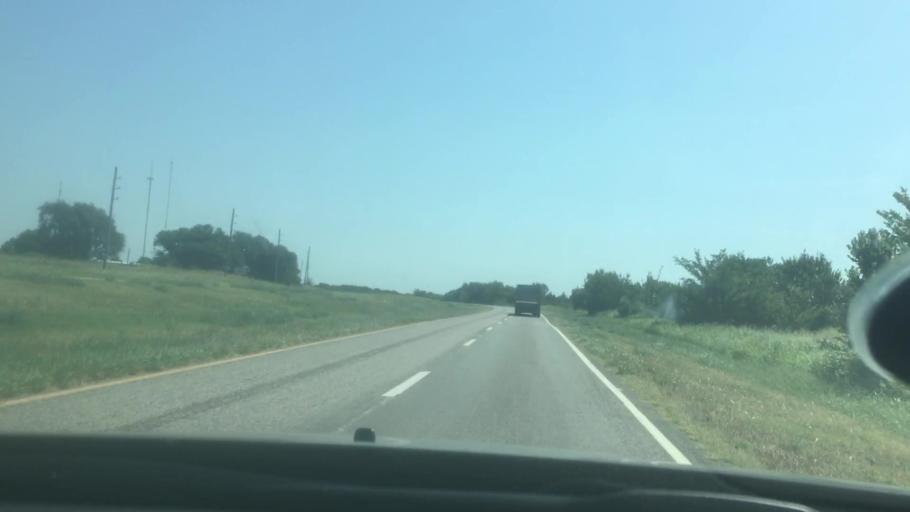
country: US
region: Oklahoma
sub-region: Pontotoc County
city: Ada
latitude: 34.7193
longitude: -96.7189
